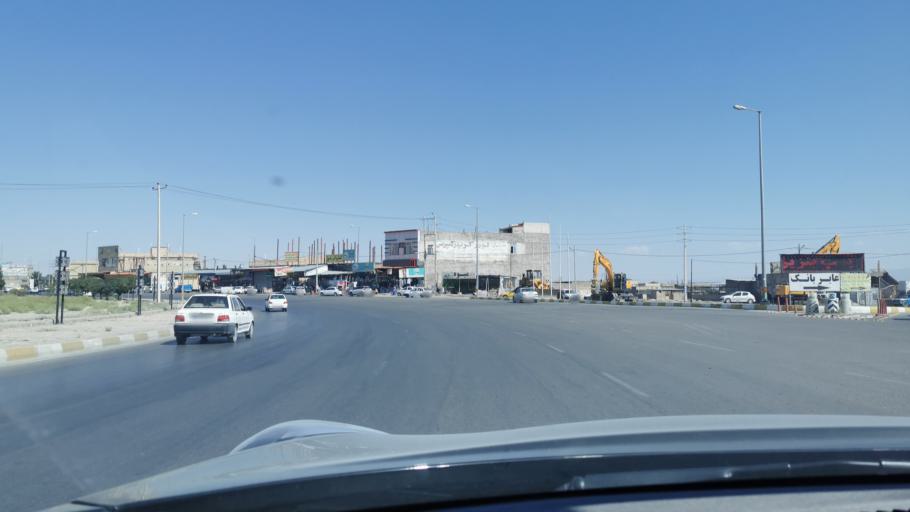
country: IR
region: Razavi Khorasan
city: Chenaran
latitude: 36.6341
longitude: 59.1322
